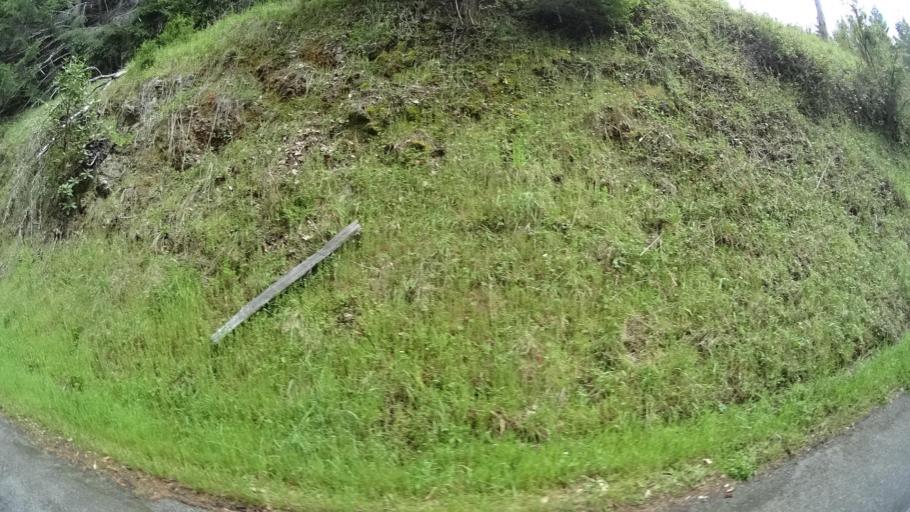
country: US
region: California
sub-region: Humboldt County
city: Blue Lake
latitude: 40.7939
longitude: -123.9777
